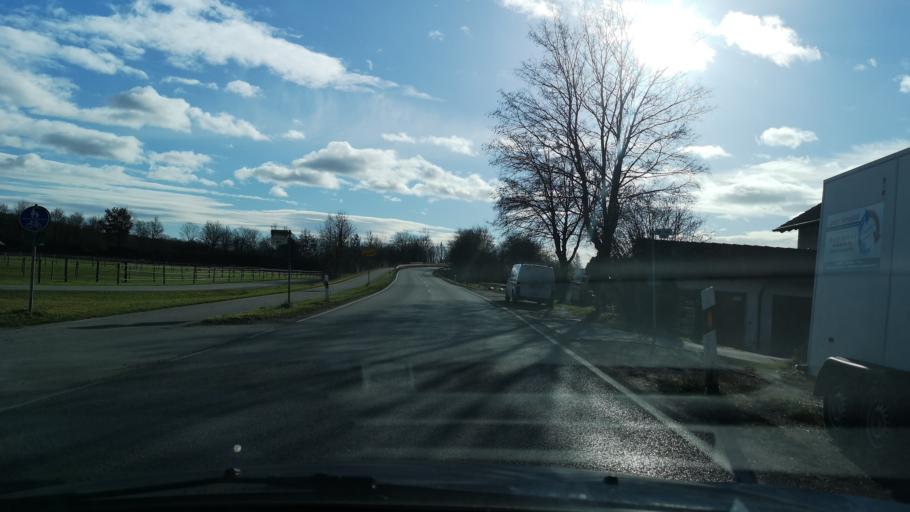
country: DE
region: Bavaria
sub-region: Upper Bavaria
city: Poing
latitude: 48.1570
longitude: 11.8172
